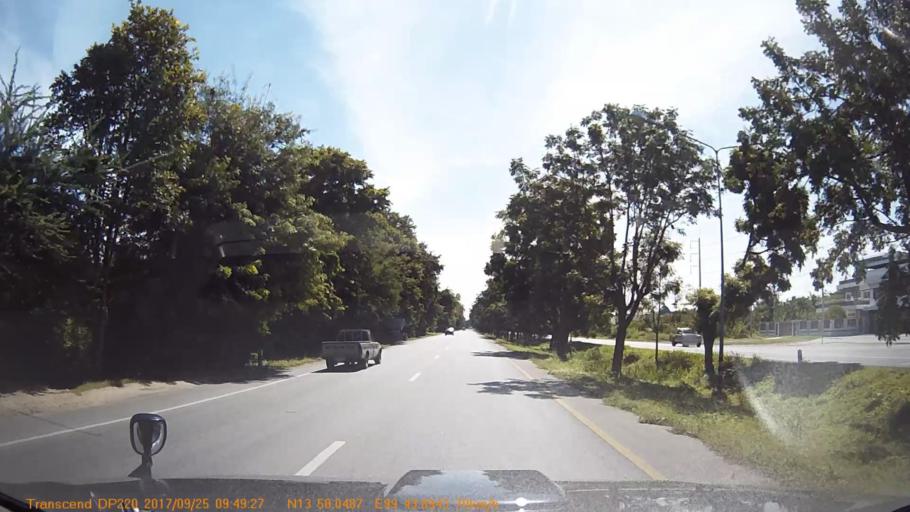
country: TH
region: Kanchanaburi
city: Tha Maka
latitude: 13.9674
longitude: 99.7320
